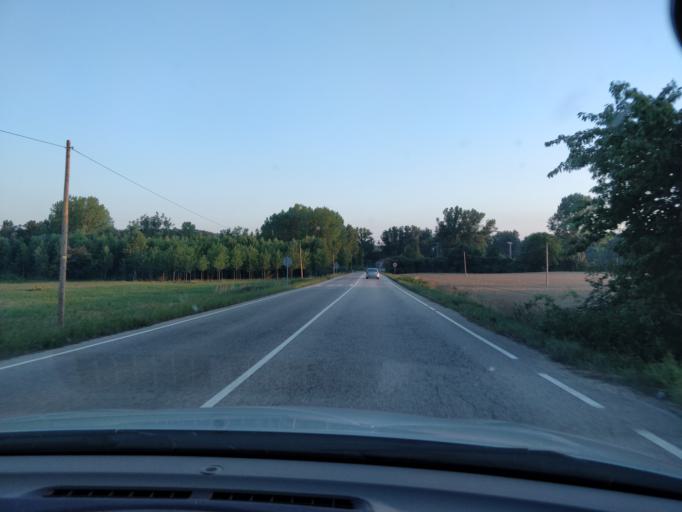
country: ES
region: Castille and Leon
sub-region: Provincia de Burgos
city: Medina de Pomar
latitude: 42.9677
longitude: -3.5461
